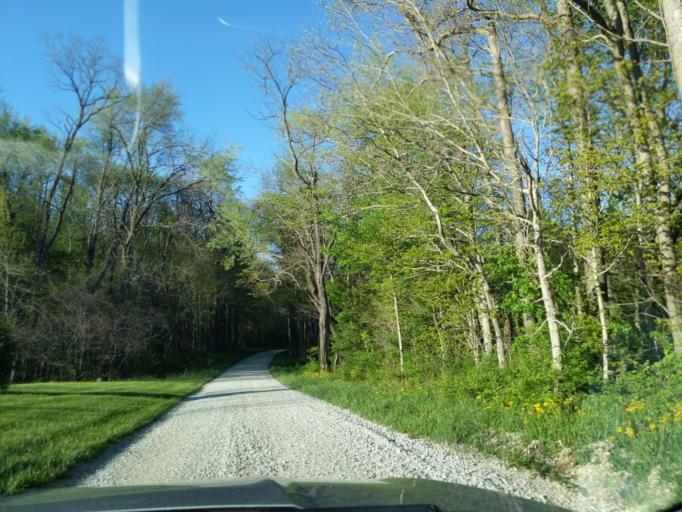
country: US
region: Indiana
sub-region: Decatur County
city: Westport
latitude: 39.1975
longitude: -85.4431
